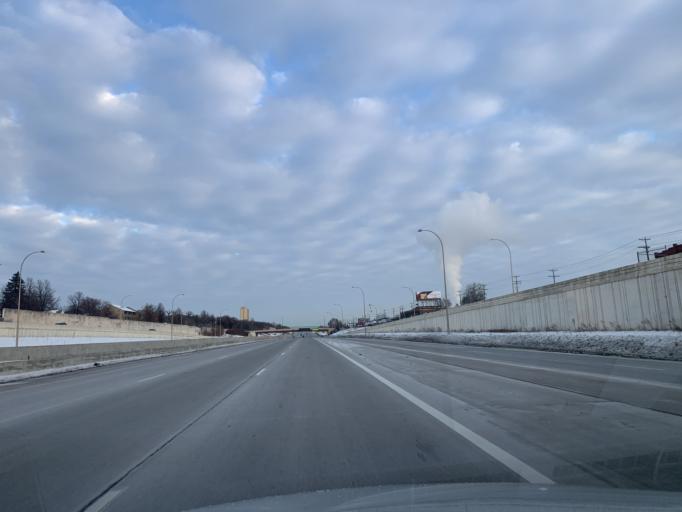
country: US
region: Minnesota
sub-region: Hennepin County
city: Minneapolis
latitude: 45.0015
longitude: -93.2825
